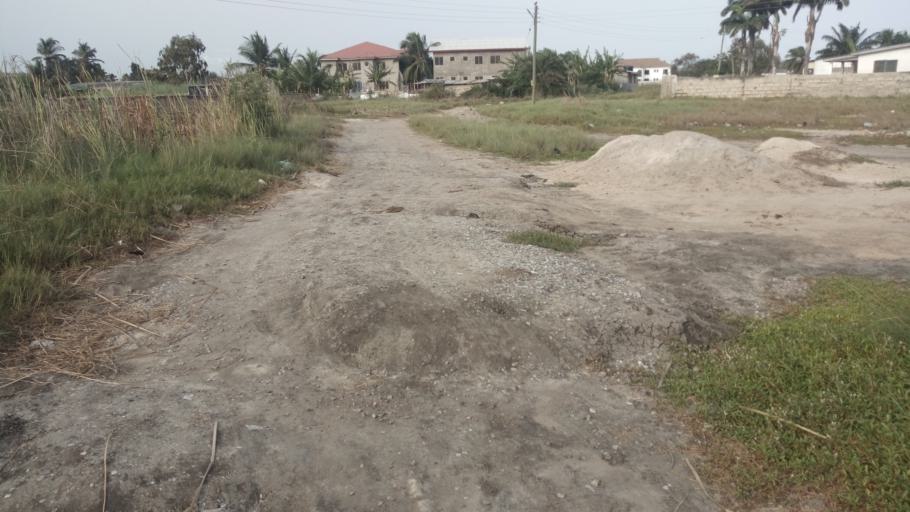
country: GH
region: Central
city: Winneba
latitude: 5.3493
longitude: -0.6355
